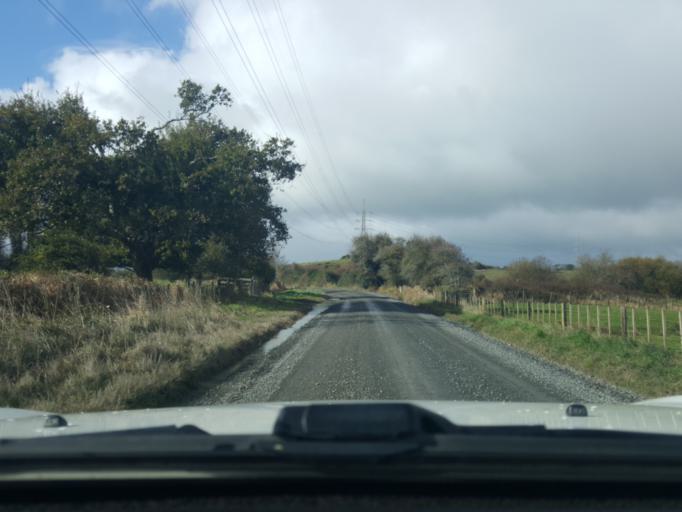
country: NZ
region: Waikato
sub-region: Waikato District
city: Te Kauwhata
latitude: -37.4204
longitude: 175.0711
